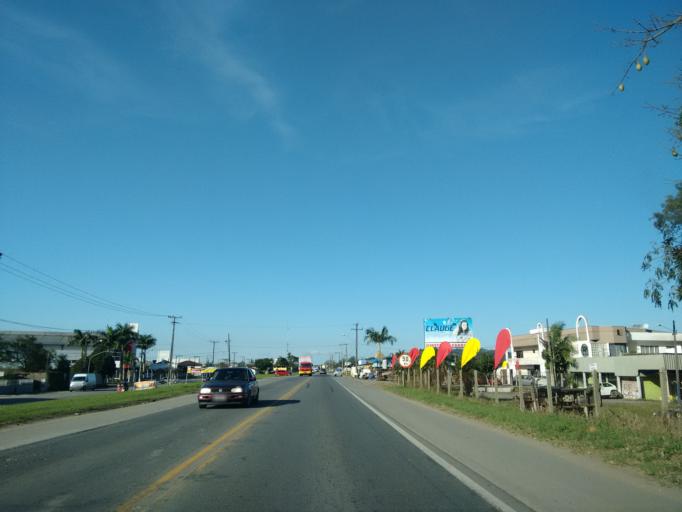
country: BR
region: Santa Catarina
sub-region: Guaramirim
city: Guaramirim
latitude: -26.4755
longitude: -48.9912
